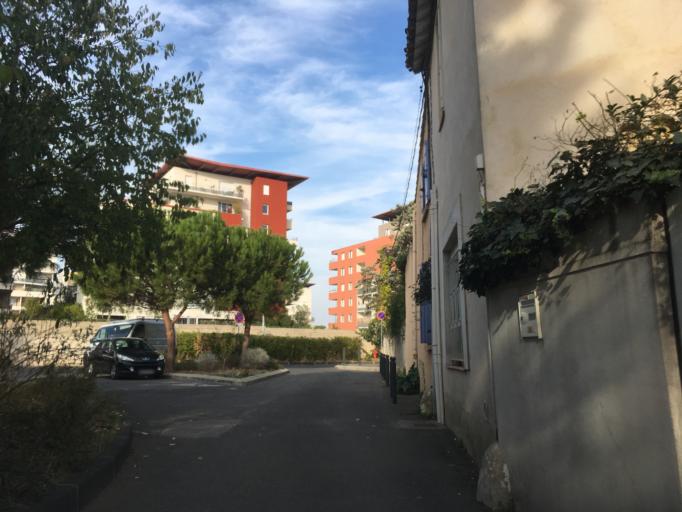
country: FR
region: Languedoc-Roussillon
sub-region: Departement de l'Herault
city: Castelnau-le-Lez
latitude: 43.6047
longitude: 3.9103
